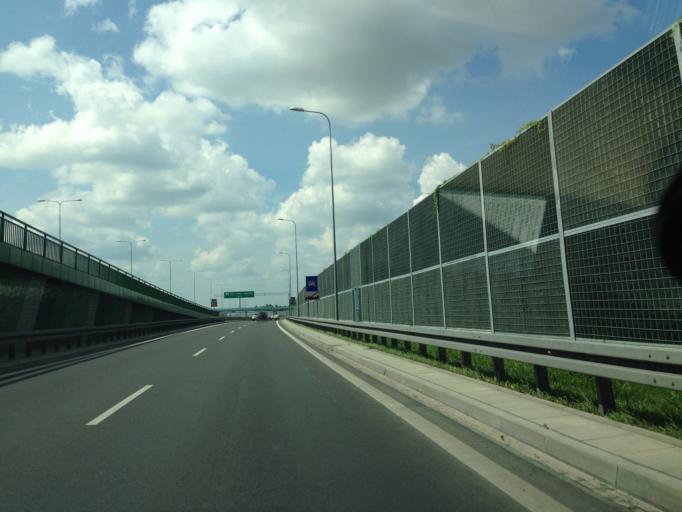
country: PL
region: Masovian Voivodeship
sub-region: Warszawa
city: Ursynow
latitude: 52.1396
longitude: 21.0146
